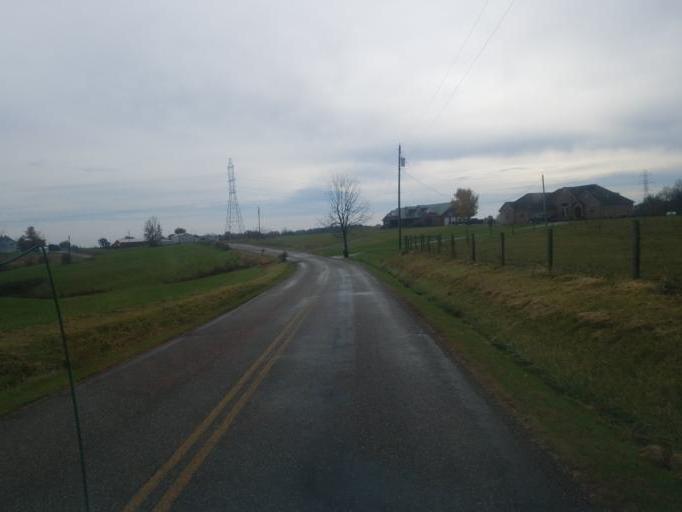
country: US
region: Ohio
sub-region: Washington County
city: Beverly
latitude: 39.5542
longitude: -81.6955
